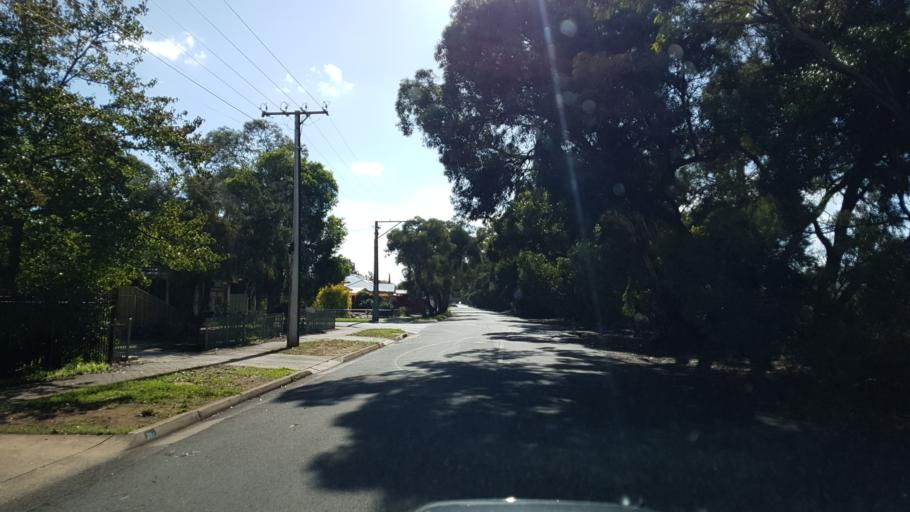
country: AU
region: South Australia
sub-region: Salisbury
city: Salisbury
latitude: -34.7509
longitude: 138.6399
